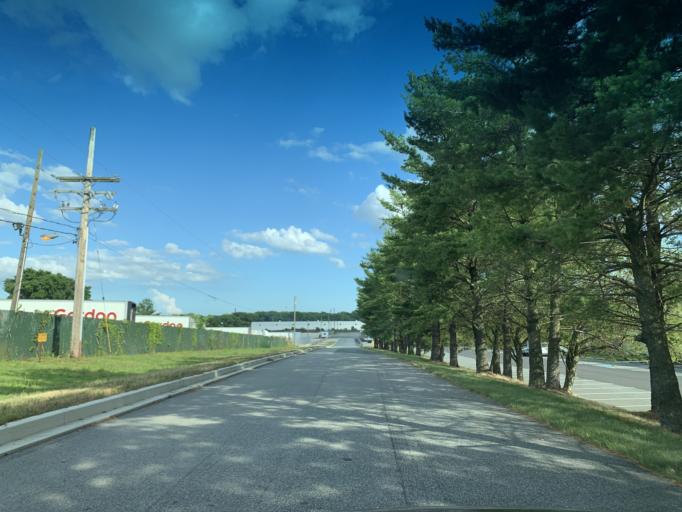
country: US
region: Maryland
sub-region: Harford County
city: Perryman
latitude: 39.4885
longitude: -76.1846
